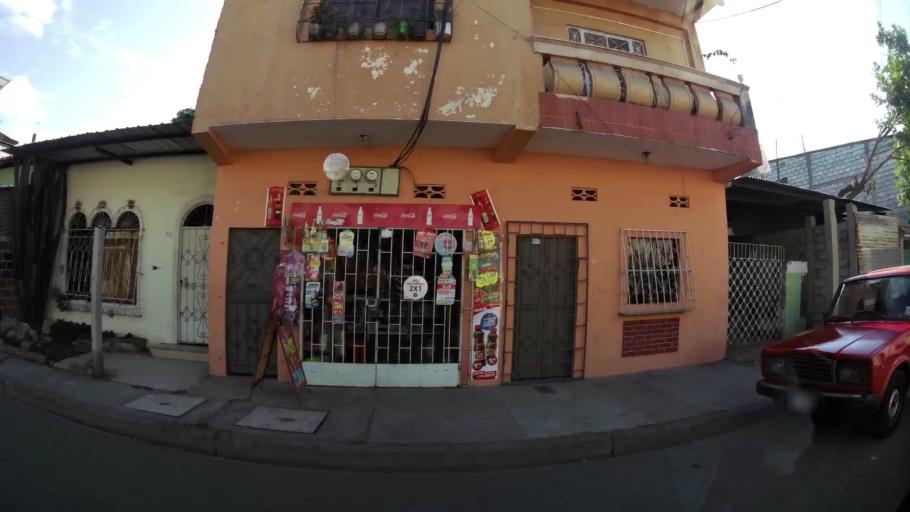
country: EC
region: Guayas
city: Guayaquil
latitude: -2.2247
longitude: -79.9272
